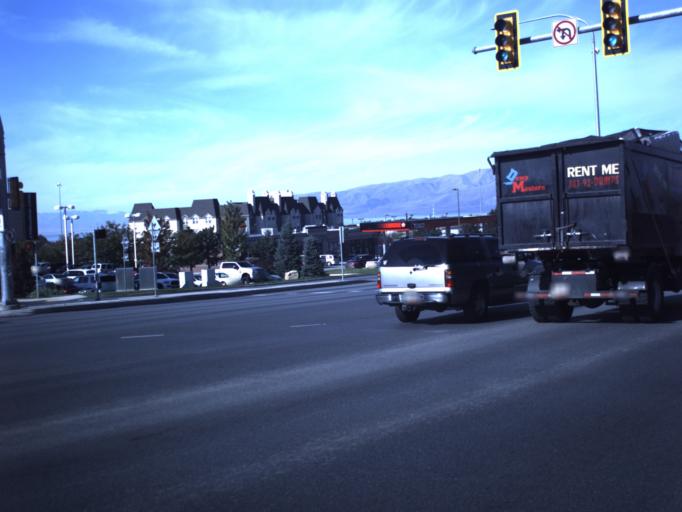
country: US
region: Utah
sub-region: Utah County
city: Orem
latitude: 40.2752
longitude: -111.7133
